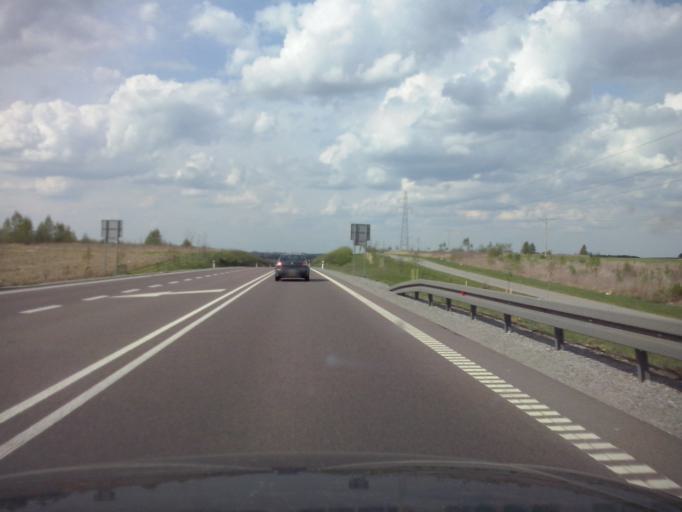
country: PL
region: Subcarpathian Voivodeship
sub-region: Powiat rzeszowski
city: Wolka Podlesna
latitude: 50.1407
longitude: 22.0790
